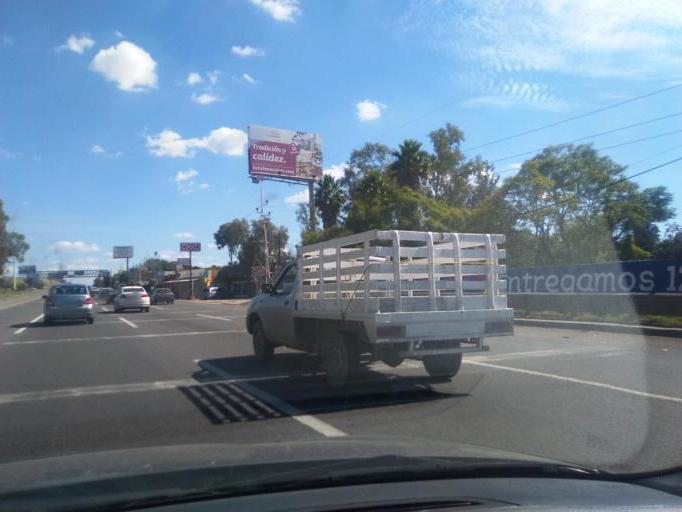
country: MX
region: Guanajuato
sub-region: Silao de la Victoria
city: El Refugio de los Sauces
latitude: 21.0264
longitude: -101.5414
